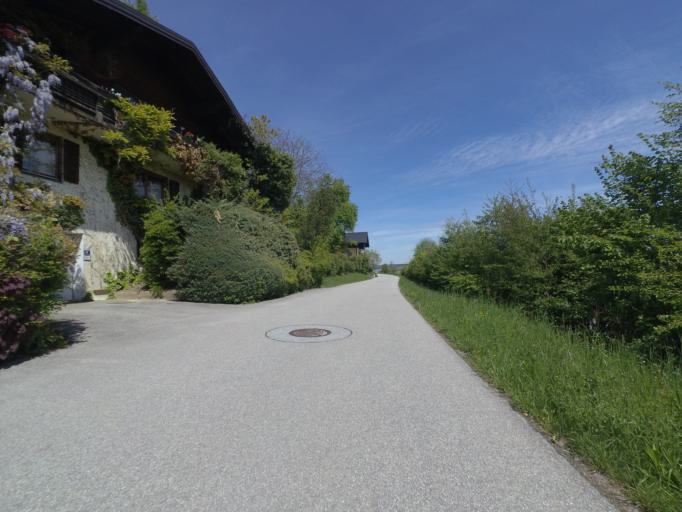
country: AT
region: Salzburg
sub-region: Politischer Bezirk Salzburg-Umgebung
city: Seeham
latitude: 47.9794
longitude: 13.0806
